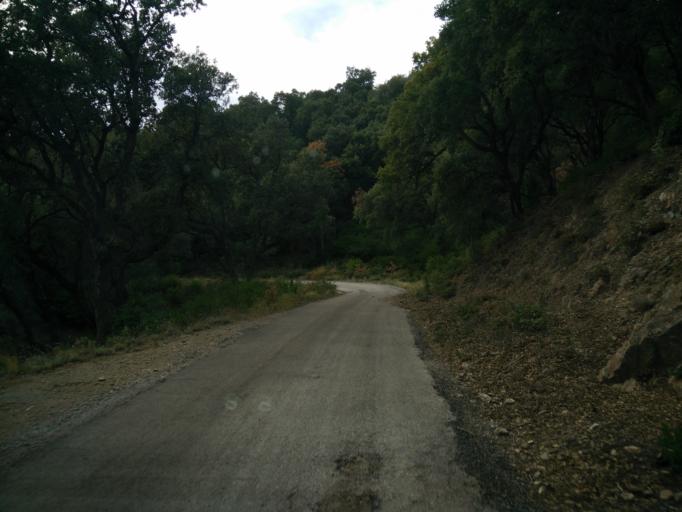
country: FR
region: Provence-Alpes-Cote d'Azur
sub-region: Departement du Var
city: Roquebrune-sur-Argens
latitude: 43.3977
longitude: 6.6141
